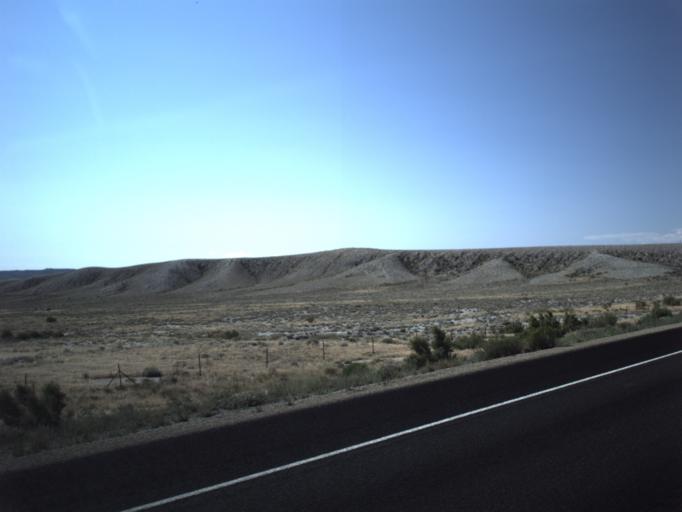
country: US
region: Utah
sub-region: Emery County
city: Ferron
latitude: 38.9826
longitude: -111.1731
